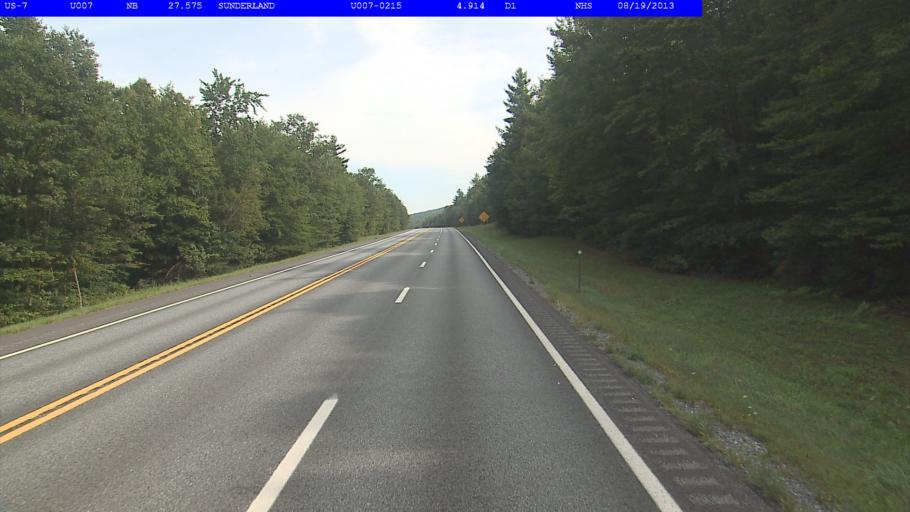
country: US
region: Vermont
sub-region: Bennington County
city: Arlington
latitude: 43.0901
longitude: -73.1026
